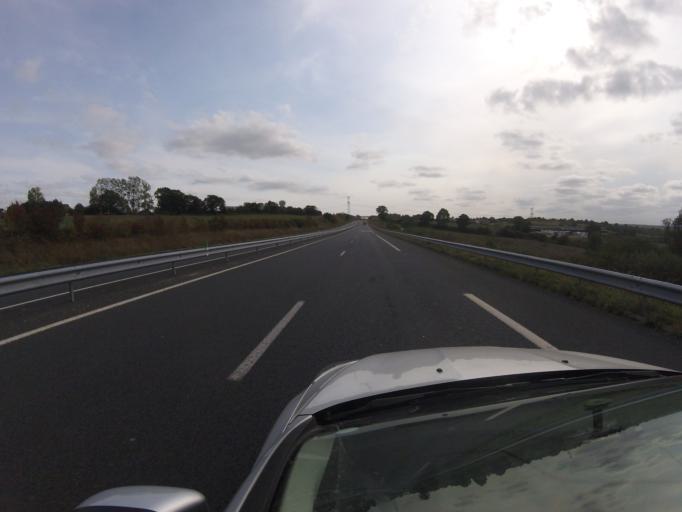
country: FR
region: Lower Normandy
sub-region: Departement de la Manche
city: Pont-Hebert
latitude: 49.1636
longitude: -1.1544
